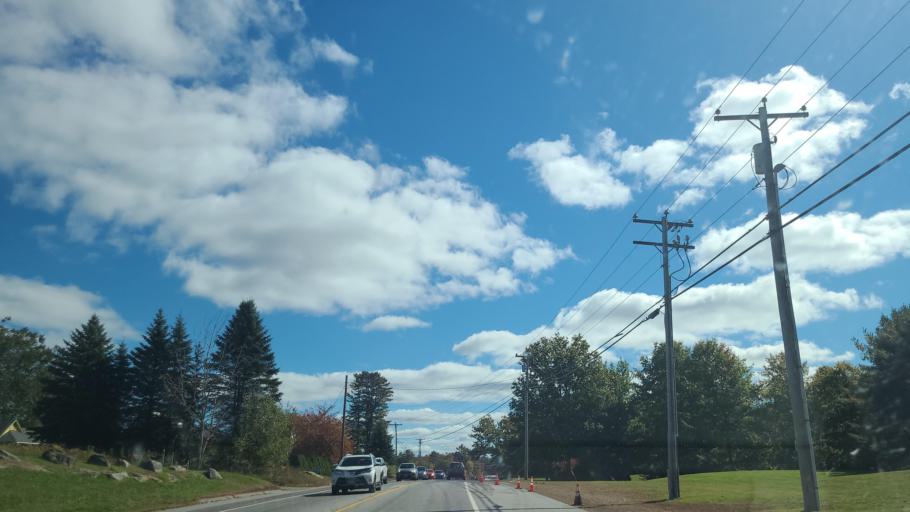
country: US
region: Maine
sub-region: Cumberland County
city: Raymond
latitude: 43.9679
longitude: -70.5863
